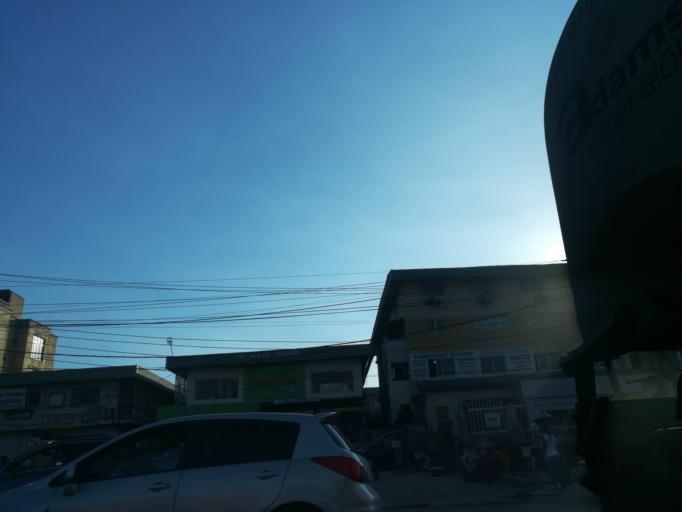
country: NG
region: Lagos
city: Ikeja
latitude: 6.6063
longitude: 3.3495
